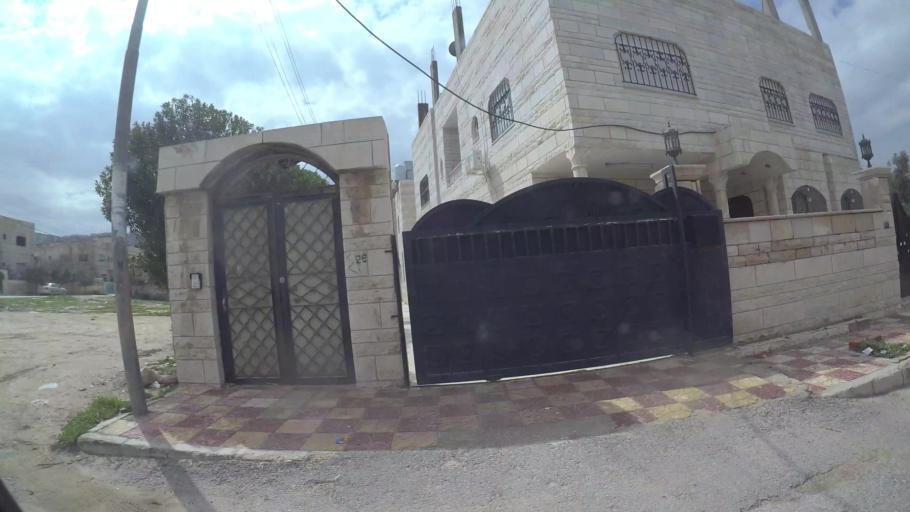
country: JO
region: Amman
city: Al Jubayhah
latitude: 32.0527
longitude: 35.8272
